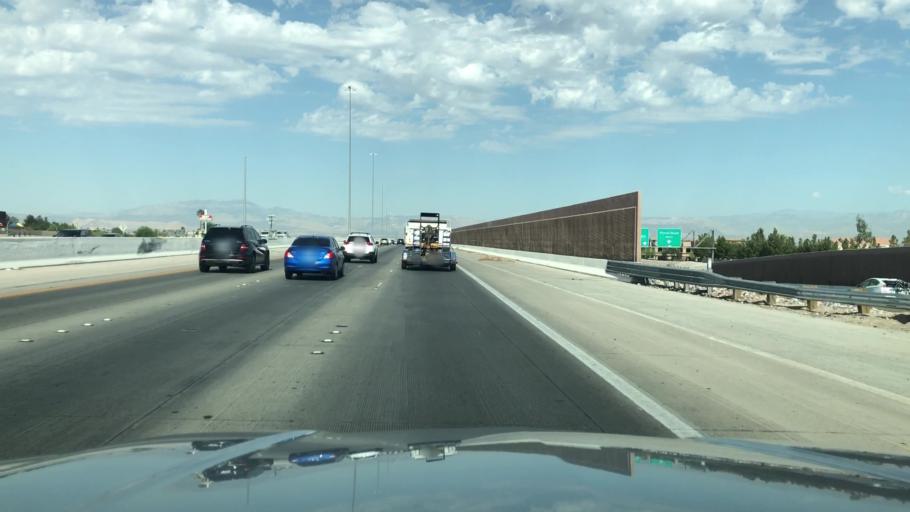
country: US
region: Nevada
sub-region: Clark County
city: Whitney
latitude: 36.0236
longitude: -115.0975
